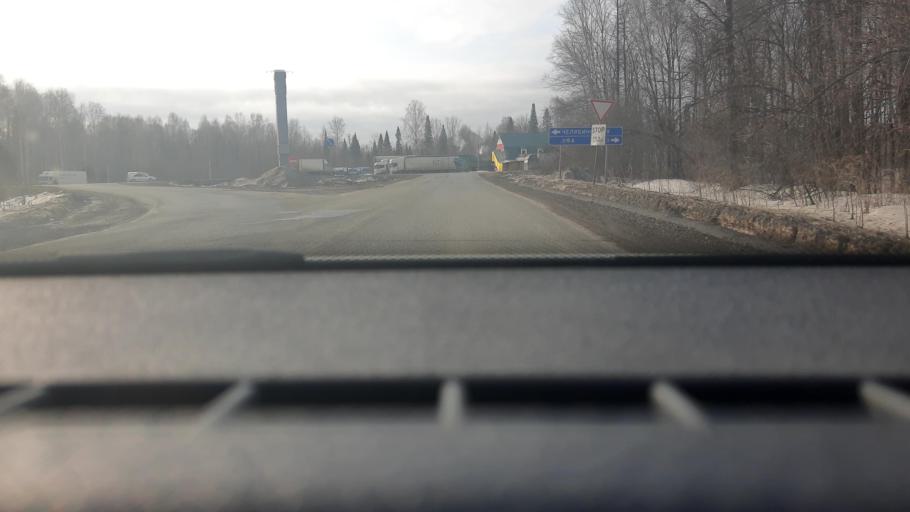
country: RU
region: Chelyabinsk
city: Asha
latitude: 54.8894
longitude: 57.3003
